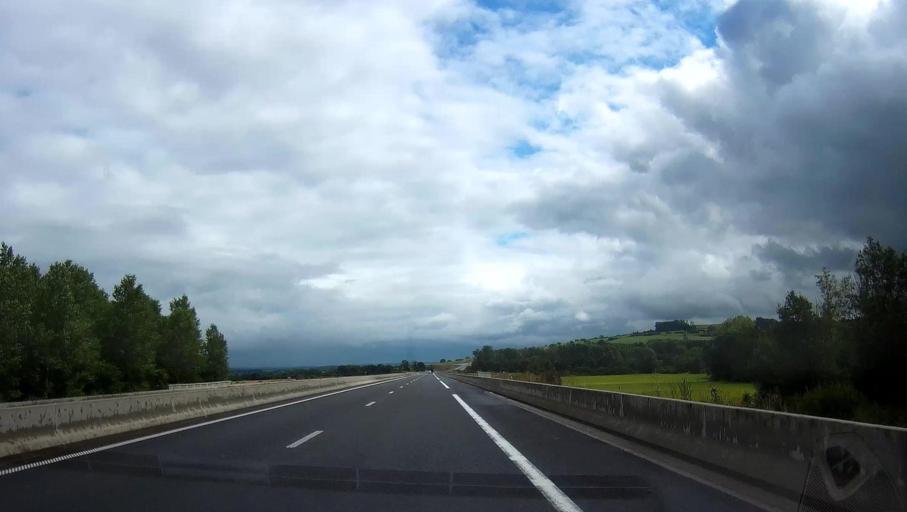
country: FR
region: Champagne-Ardenne
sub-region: Departement des Ardennes
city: Renwez
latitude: 49.7864
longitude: 4.5818
